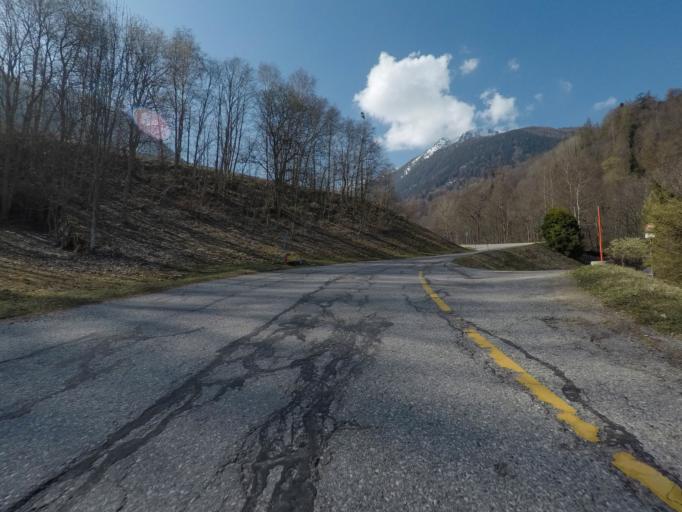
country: CH
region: Valais
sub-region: Conthey District
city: Basse-Nendaz
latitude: 46.1773
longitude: 7.3245
